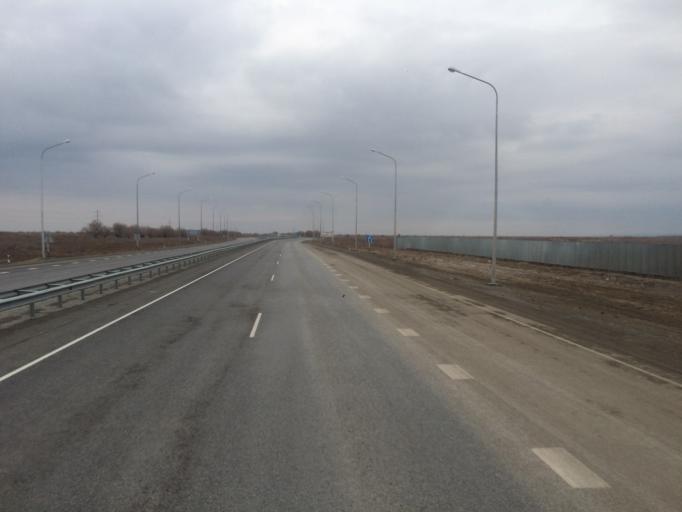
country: KZ
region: Qyzylorda
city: Shieli
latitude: 44.1409
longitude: 66.9633
